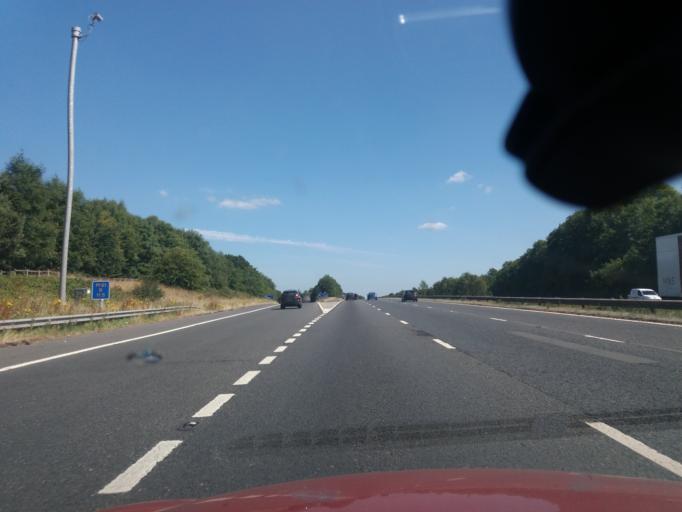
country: GB
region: England
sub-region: Borough of Bolton
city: Westhoughton
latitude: 53.5574
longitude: -2.4948
